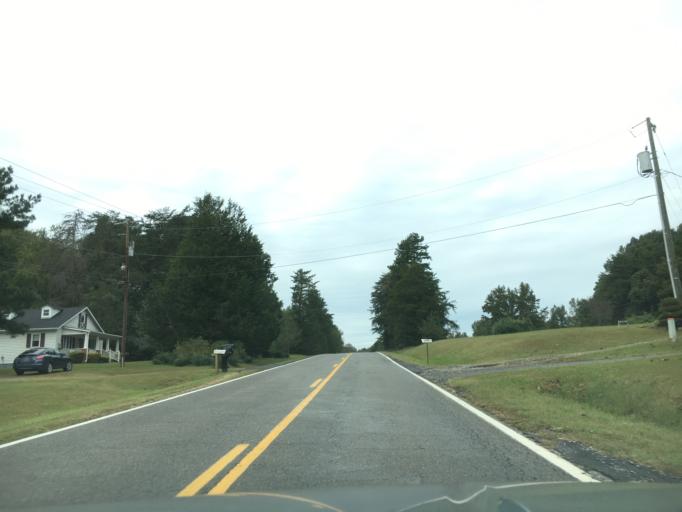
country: US
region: Virginia
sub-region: Goochland County
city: Goochland
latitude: 37.7656
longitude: -77.8819
